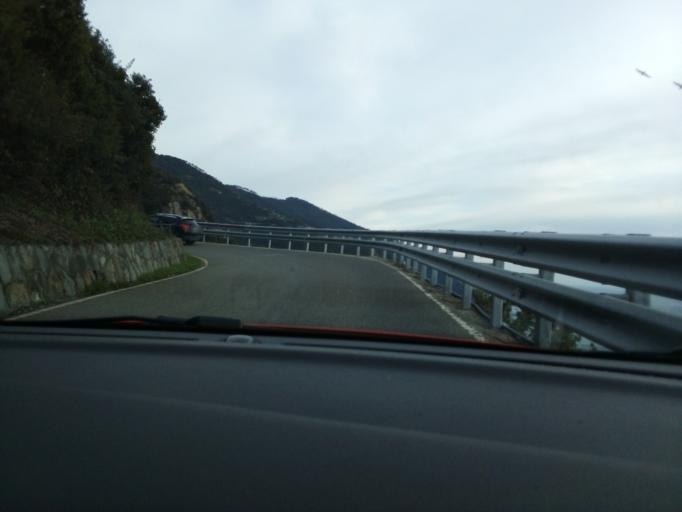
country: IT
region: Liguria
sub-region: Provincia di La Spezia
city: Riomaggiore
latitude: 44.0934
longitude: 9.7428
